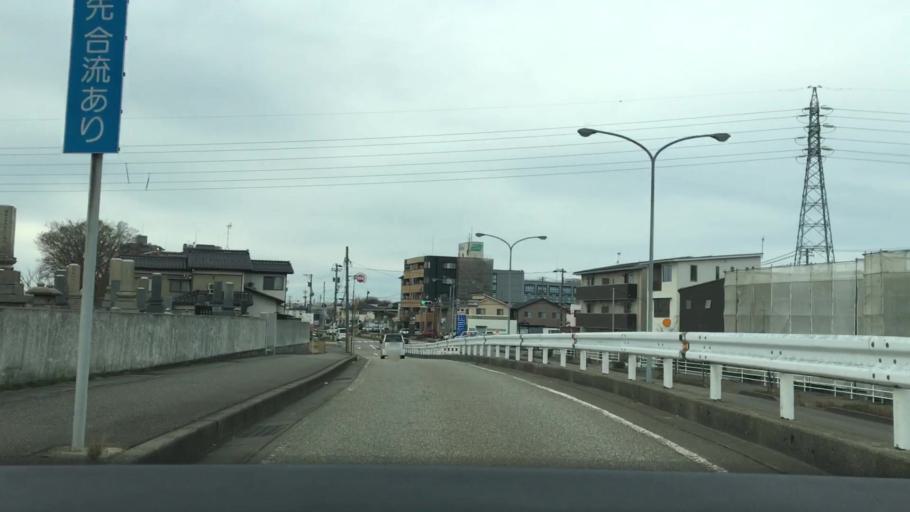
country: JP
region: Ishikawa
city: Kanazawa-shi
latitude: 36.5753
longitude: 136.6257
